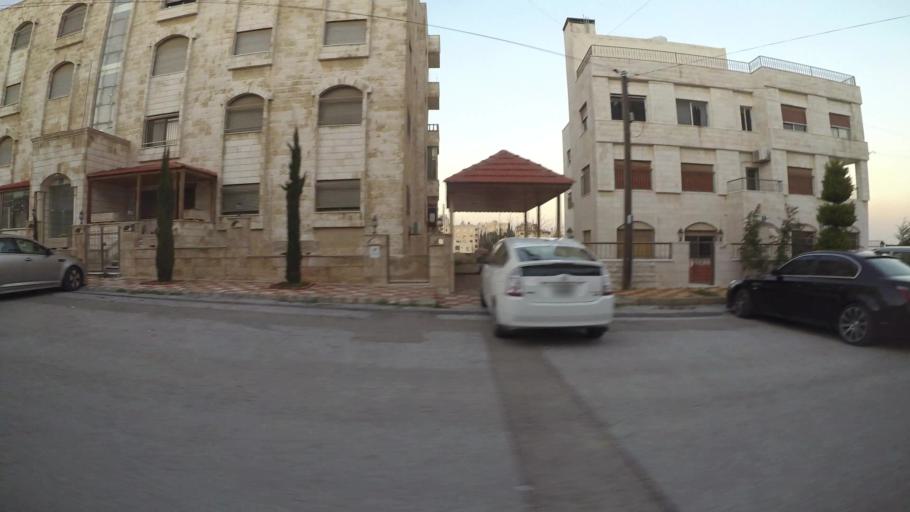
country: JO
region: Amman
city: Al Jubayhah
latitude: 31.9992
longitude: 35.8563
